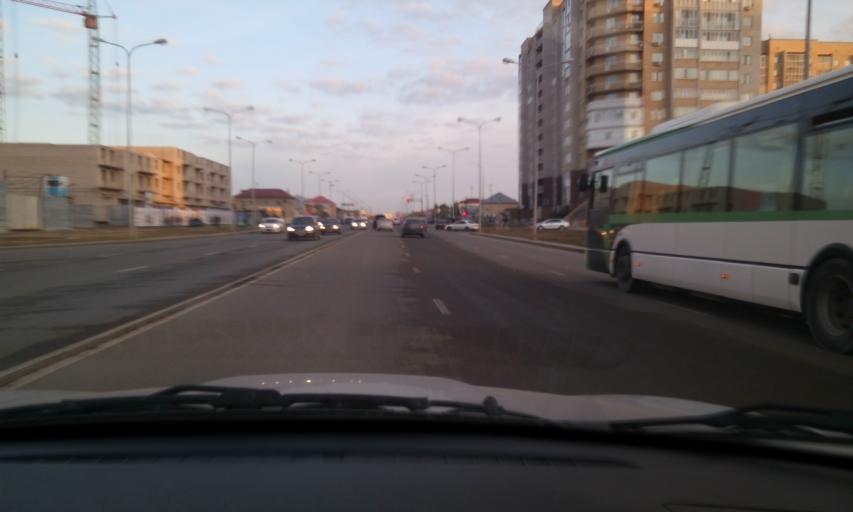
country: KZ
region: Astana Qalasy
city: Astana
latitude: 51.1297
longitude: 71.4969
